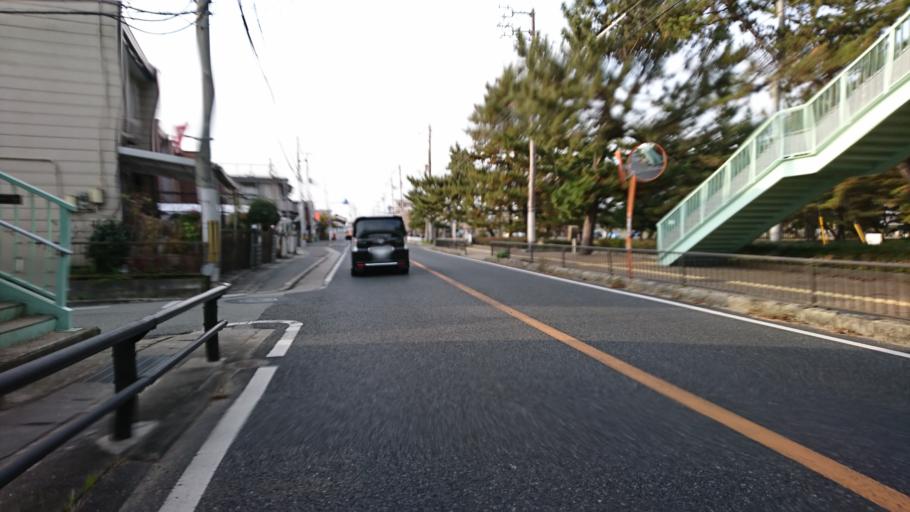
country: JP
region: Hyogo
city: Kakogawacho-honmachi
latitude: 34.7344
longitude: 134.8311
